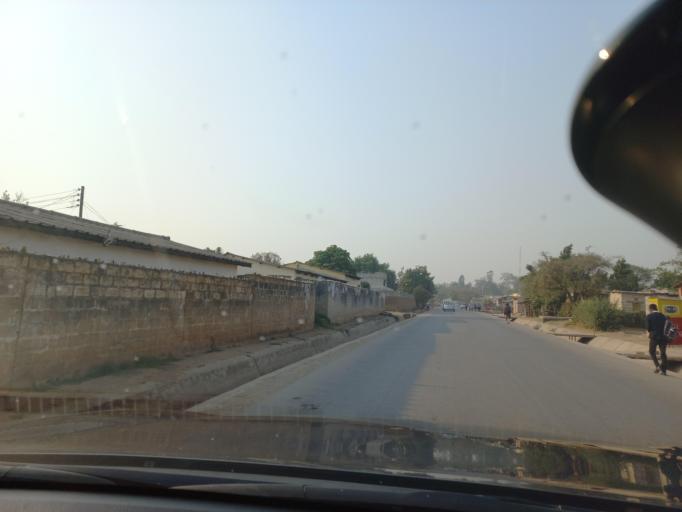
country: ZM
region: Lusaka
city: Lusaka
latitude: -15.4056
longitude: 28.3453
